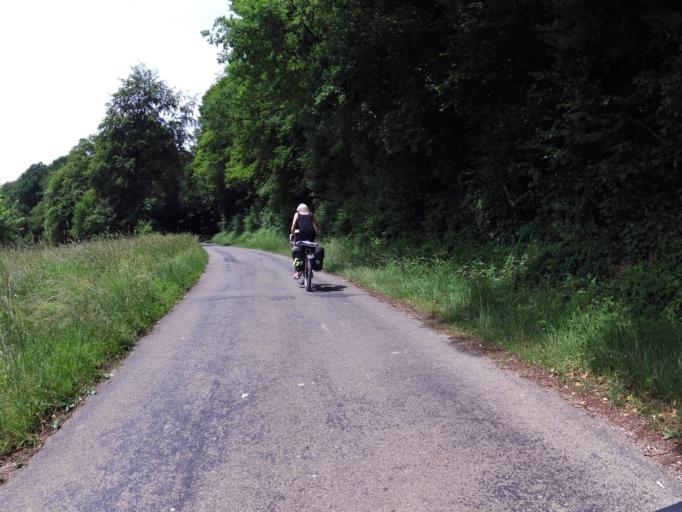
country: FR
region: Lorraine
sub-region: Departement de la Meuse
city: Stenay
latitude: 49.5371
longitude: 5.1501
